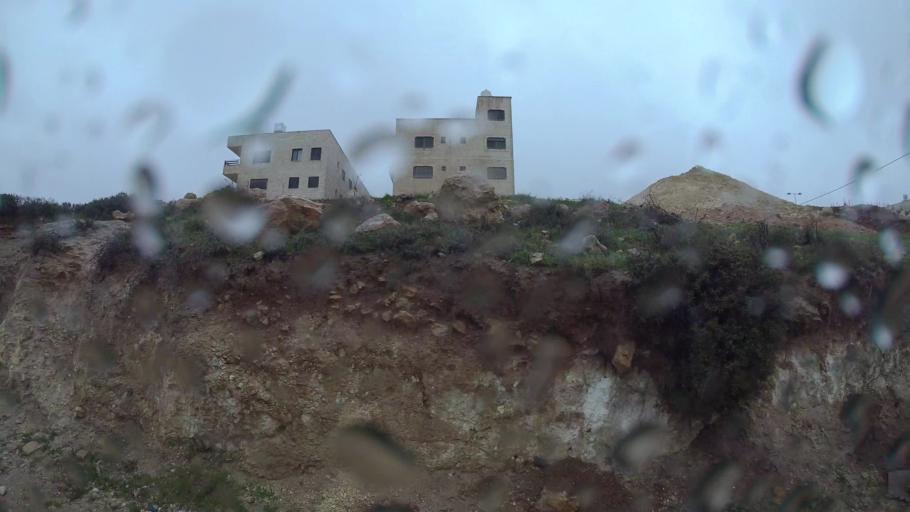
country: JO
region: Amman
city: Al Jubayhah
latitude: 32.0366
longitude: 35.8844
